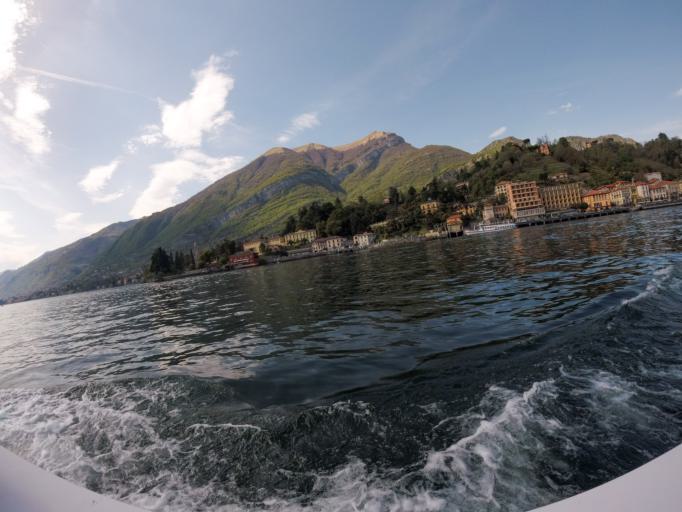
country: IT
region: Lombardy
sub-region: Provincia di Como
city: Tremezzo
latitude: 45.9812
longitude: 9.2264
